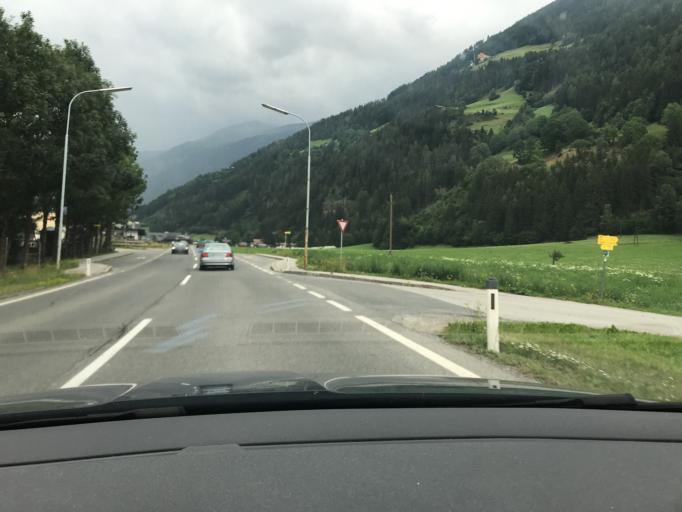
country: AT
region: Tyrol
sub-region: Politischer Bezirk Lienz
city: Matrei in Osttirol
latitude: 46.9767
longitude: 12.5505
